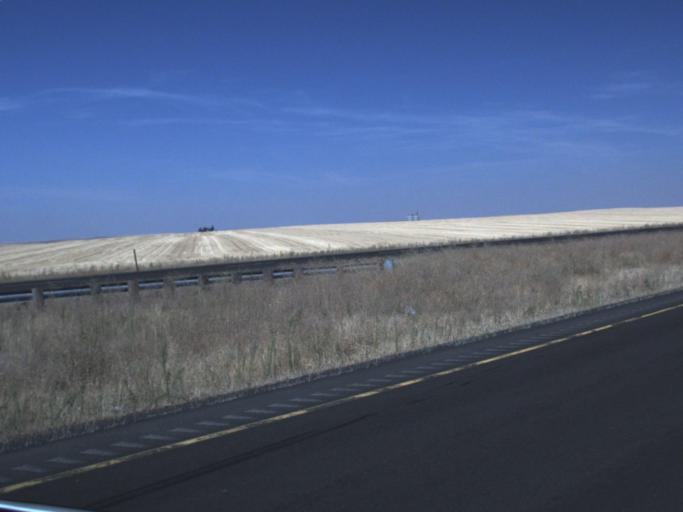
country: US
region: Washington
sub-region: Adams County
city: Ritzville
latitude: 47.1257
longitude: -118.3523
